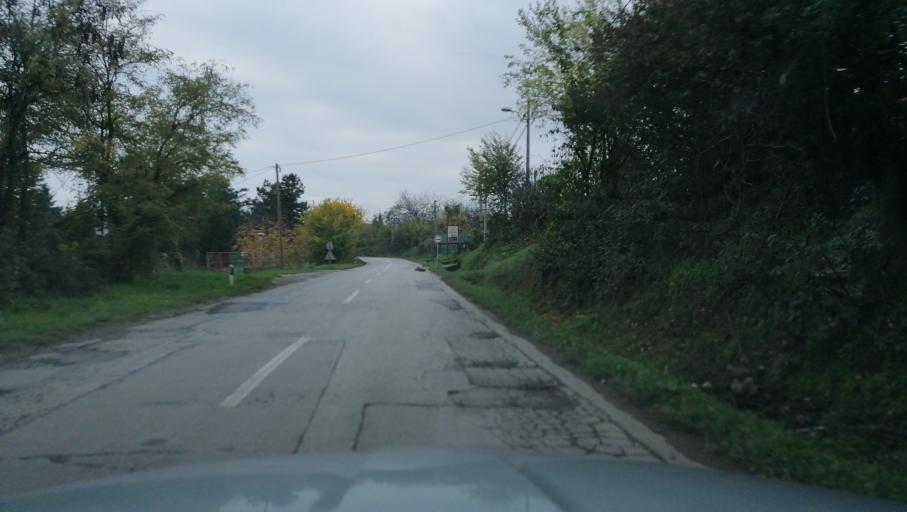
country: RS
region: Central Serbia
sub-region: Podunavski Okrug
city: Smederevo
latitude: 44.6568
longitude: 20.8721
